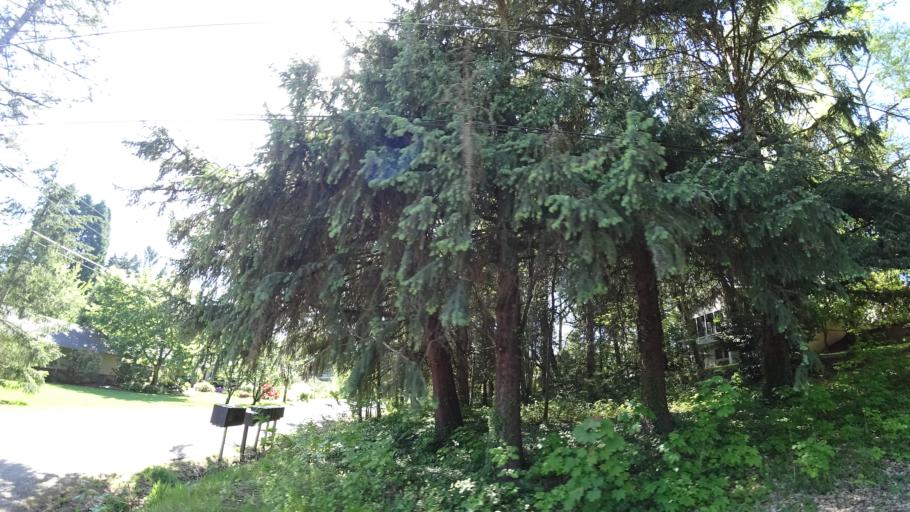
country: US
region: Oregon
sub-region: Washington County
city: Raleigh Hills
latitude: 45.4891
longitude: -122.7395
